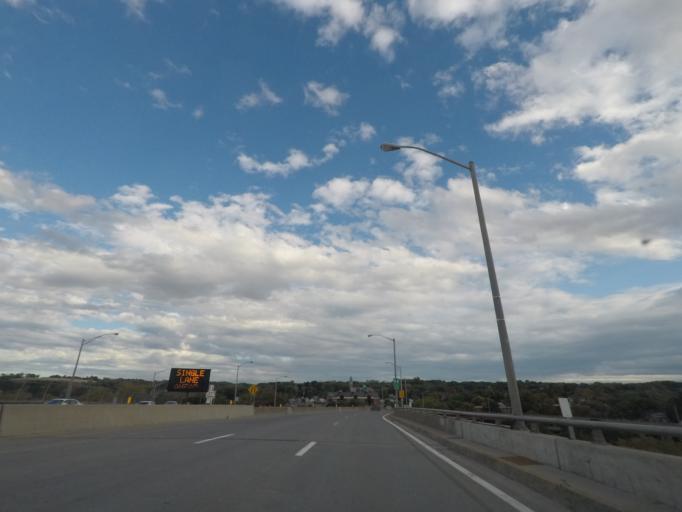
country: US
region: New York
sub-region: Rensselaer County
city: Rensselaer
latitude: 42.6428
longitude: -73.7470
